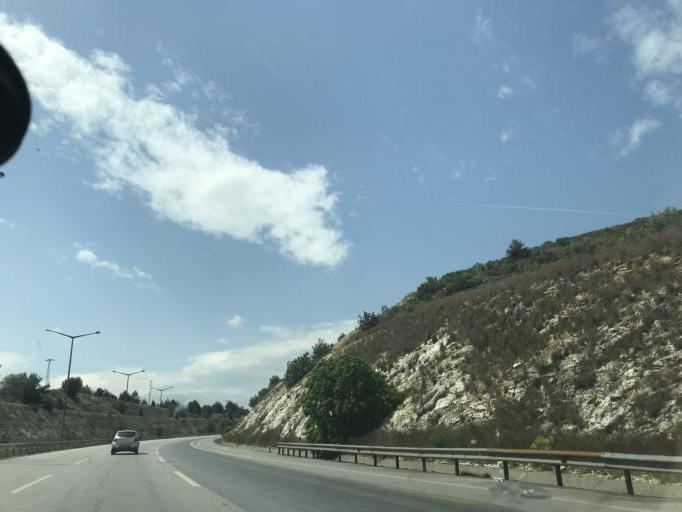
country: TR
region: Mersin
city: Tarsus
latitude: 37.1367
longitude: 34.8475
